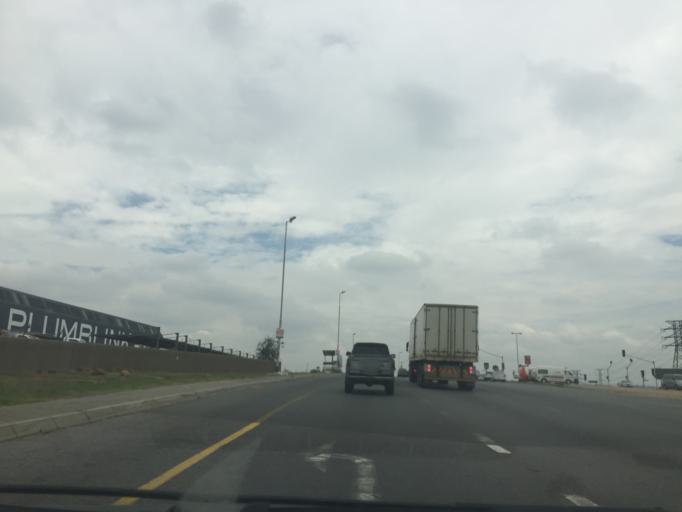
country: ZA
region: Gauteng
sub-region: City of Johannesburg Metropolitan Municipality
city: Midrand
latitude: -26.0180
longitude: 28.1215
